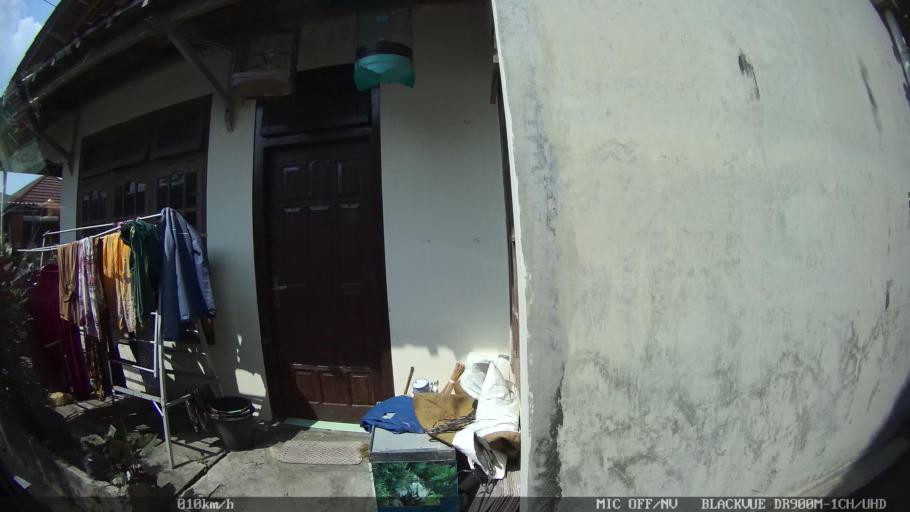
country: ID
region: Daerah Istimewa Yogyakarta
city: Yogyakarta
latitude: -7.8061
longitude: 110.4035
